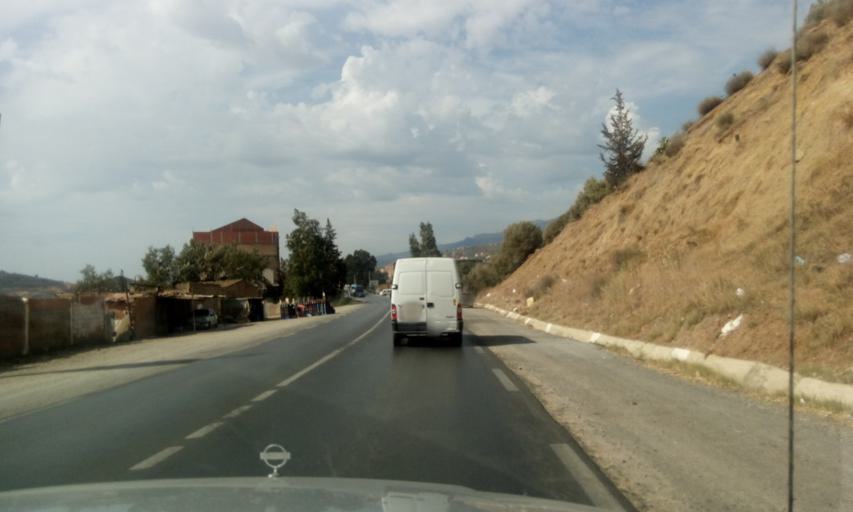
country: DZ
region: Bejaia
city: Seddouk
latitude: 36.5936
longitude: 4.6724
